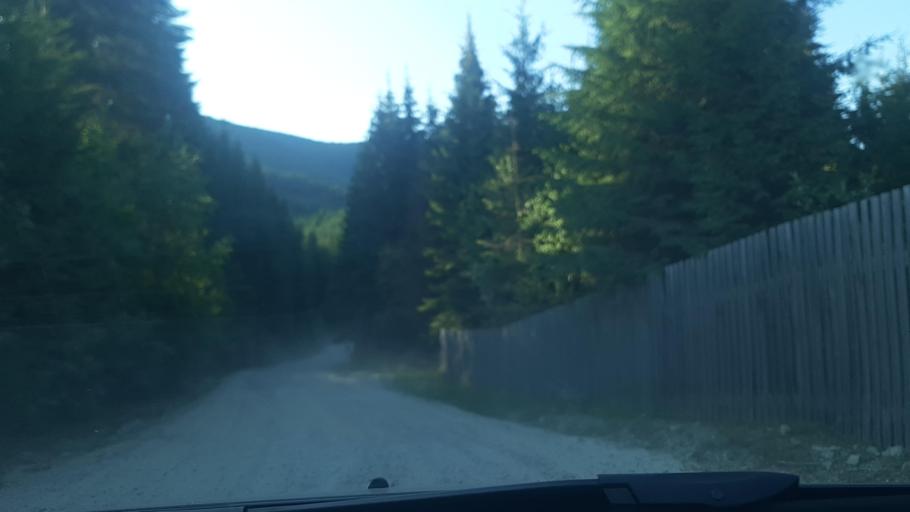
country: RO
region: Alba
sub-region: Comuna Sugag
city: Sugag
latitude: 45.5805
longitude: 23.6095
